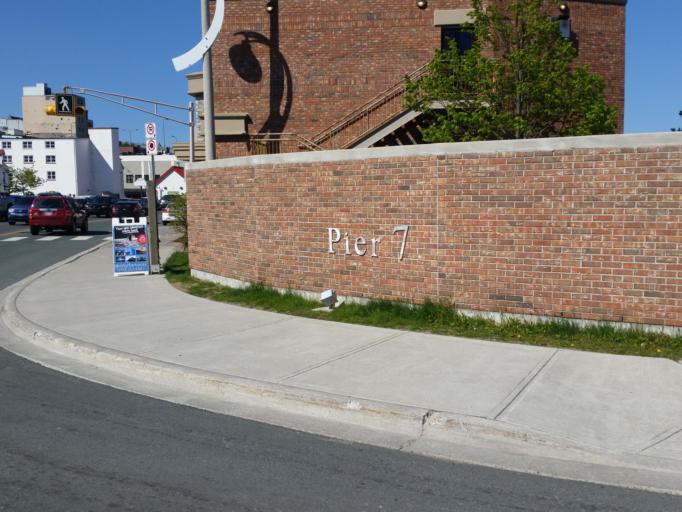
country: CA
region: Newfoundland and Labrador
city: St. John's
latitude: 47.5604
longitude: -52.7095
